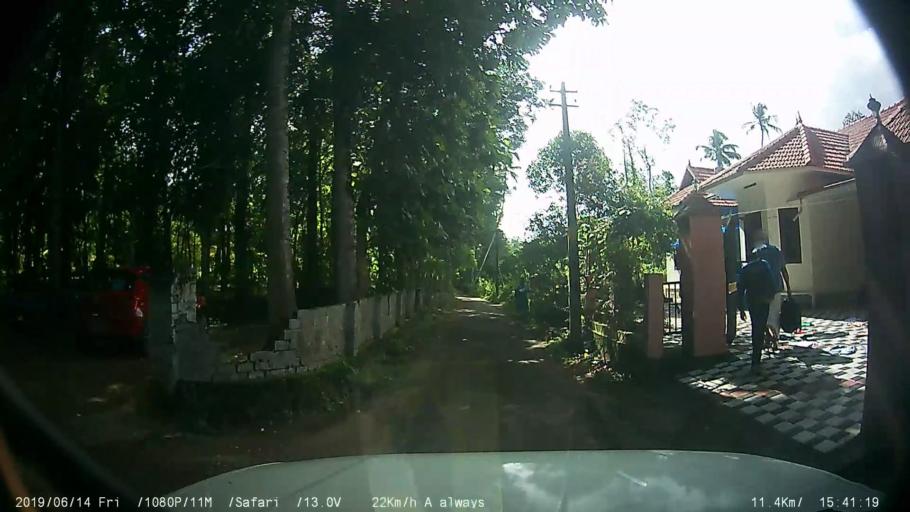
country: IN
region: Kerala
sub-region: Kottayam
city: Palackattumala
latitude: 9.7757
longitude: 76.6125
